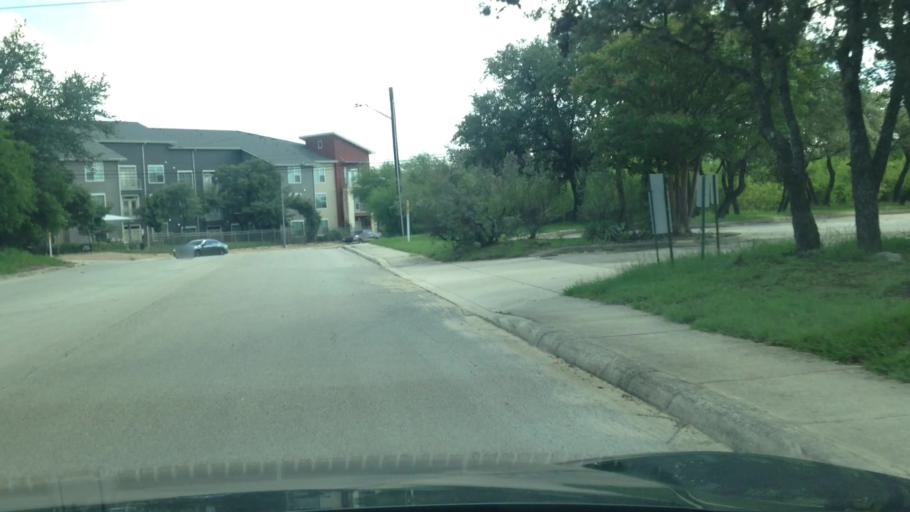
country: US
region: Texas
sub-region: Bexar County
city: Shavano Park
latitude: 29.5443
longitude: -98.5864
